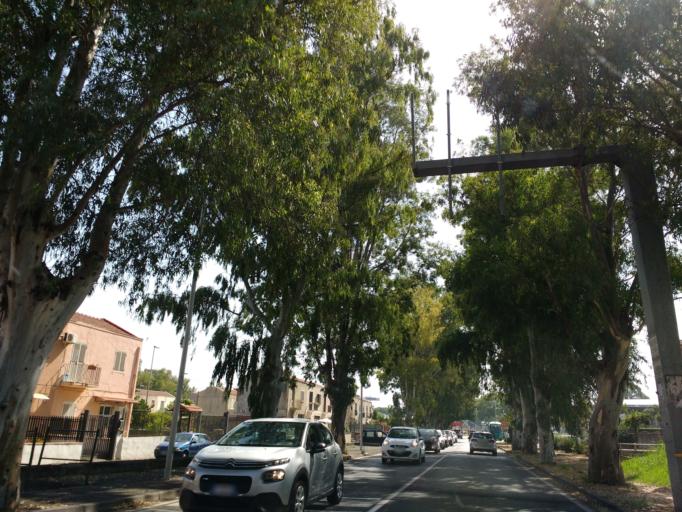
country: IT
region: Sicily
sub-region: Catania
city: Catania
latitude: 37.4741
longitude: 15.0731
